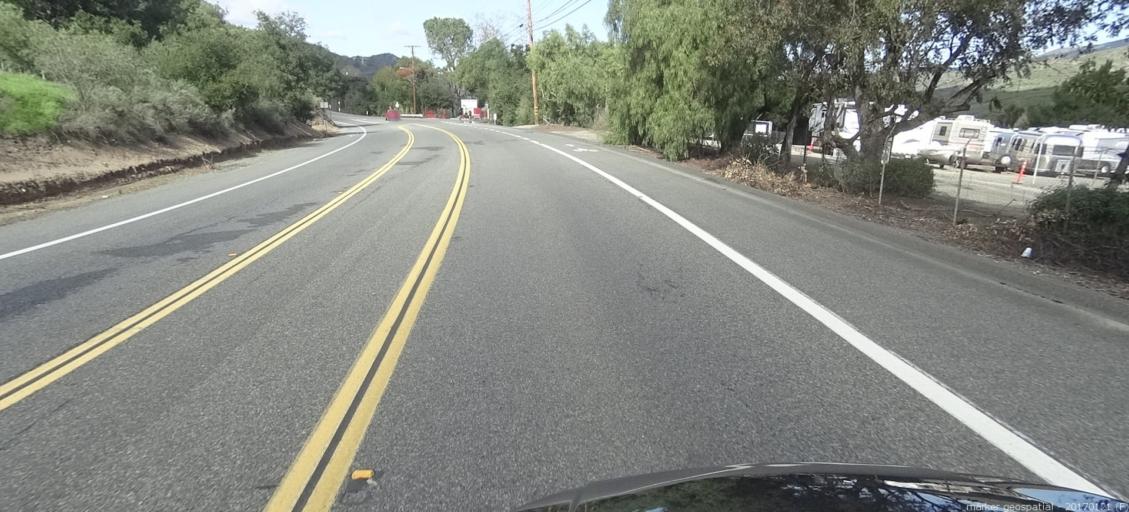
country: US
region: California
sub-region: Orange County
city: North Tustin
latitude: 33.7663
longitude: -117.7152
